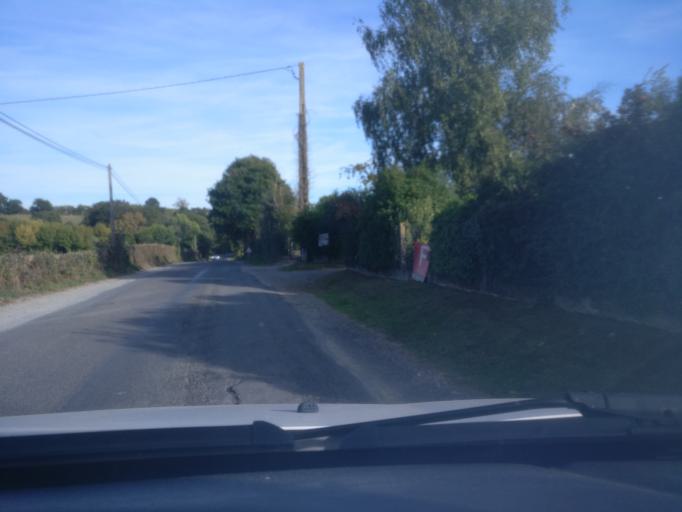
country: FR
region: Lower Normandy
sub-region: Departement de la Manche
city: Sartilly
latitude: 48.7099
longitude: -1.4855
